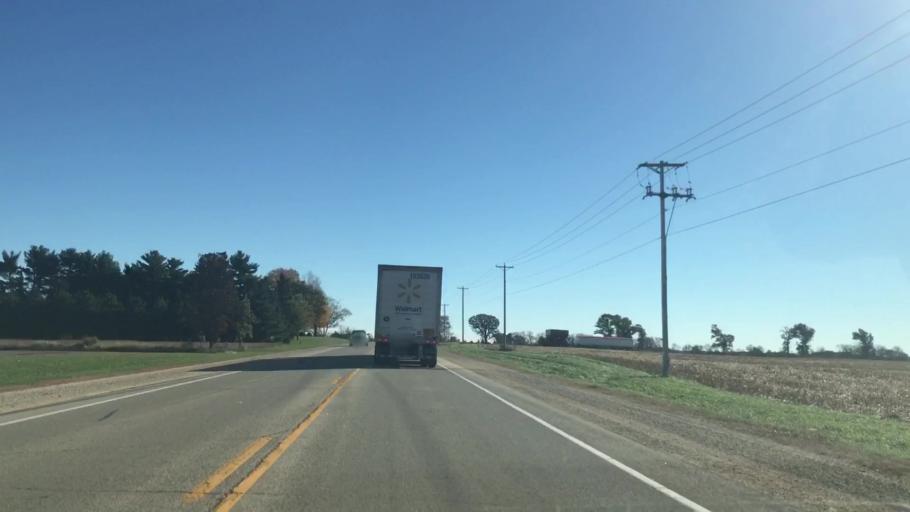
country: US
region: Wisconsin
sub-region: Dodge County
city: Juneau
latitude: 43.4447
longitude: -88.6908
